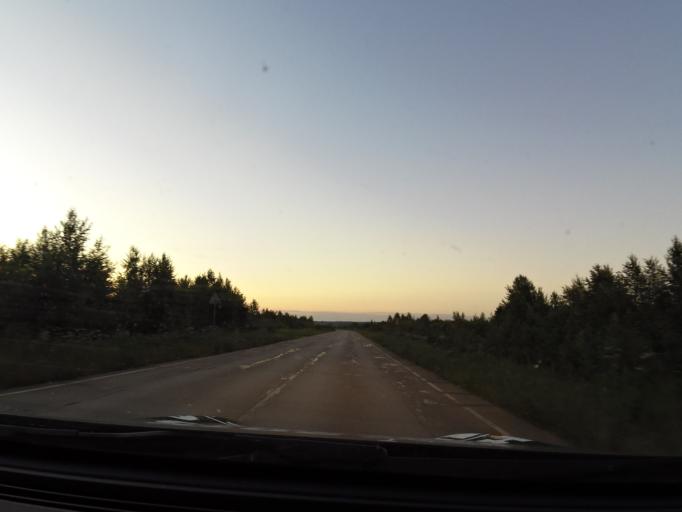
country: RU
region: Vologda
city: Vytegra
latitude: 60.8877
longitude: 36.0426
